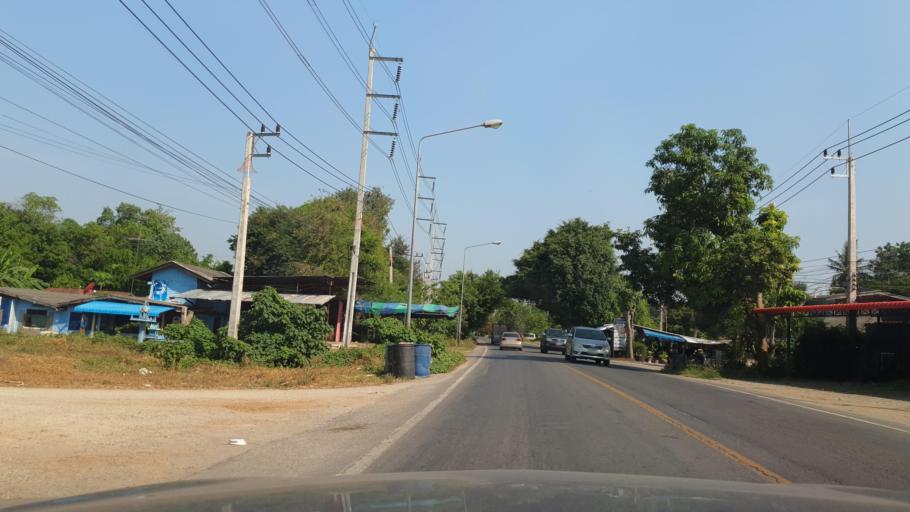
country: TH
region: Kanchanaburi
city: Kanchanaburi
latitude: 14.0426
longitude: 99.4736
